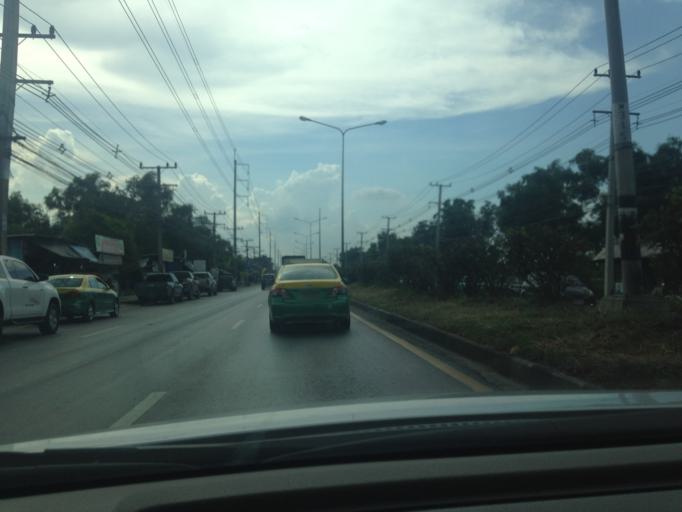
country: TH
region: Pathum Thani
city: Khlong Luang
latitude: 14.0666
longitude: 100.6848
